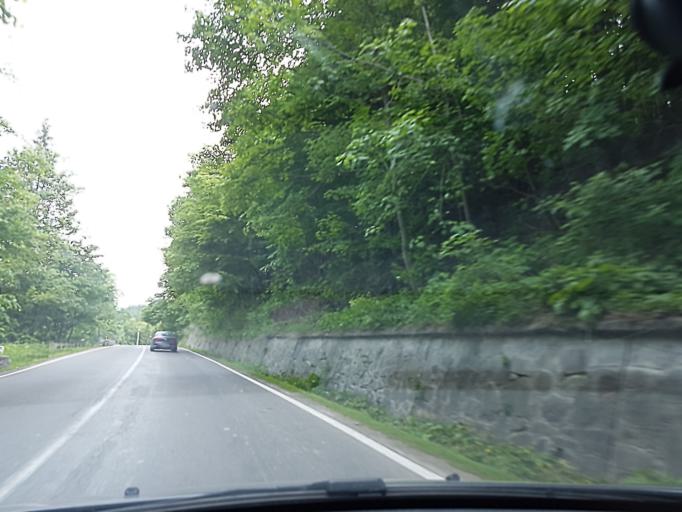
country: RO
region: Prahova
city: Maneciu
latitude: 45.3683
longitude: 25.9295
